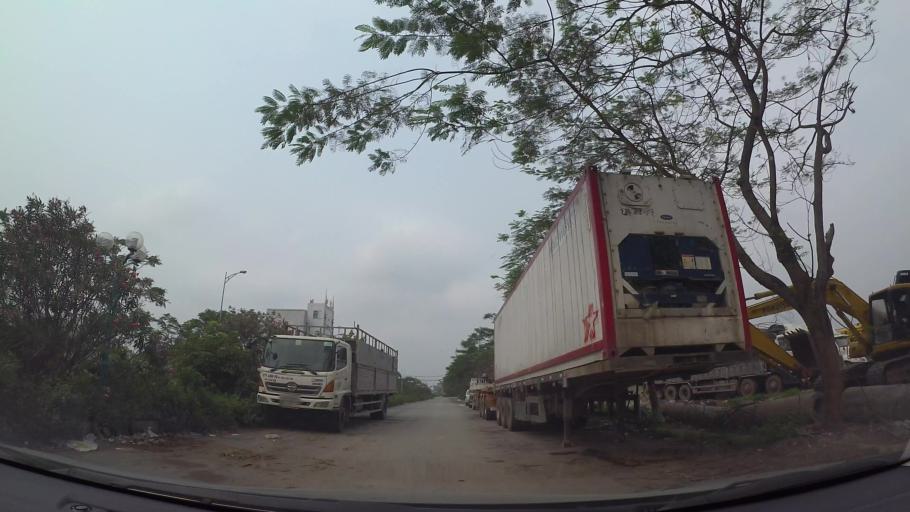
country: VN
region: Ha Noi
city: Trau Quy
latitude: 21.0660
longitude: 105.9000
